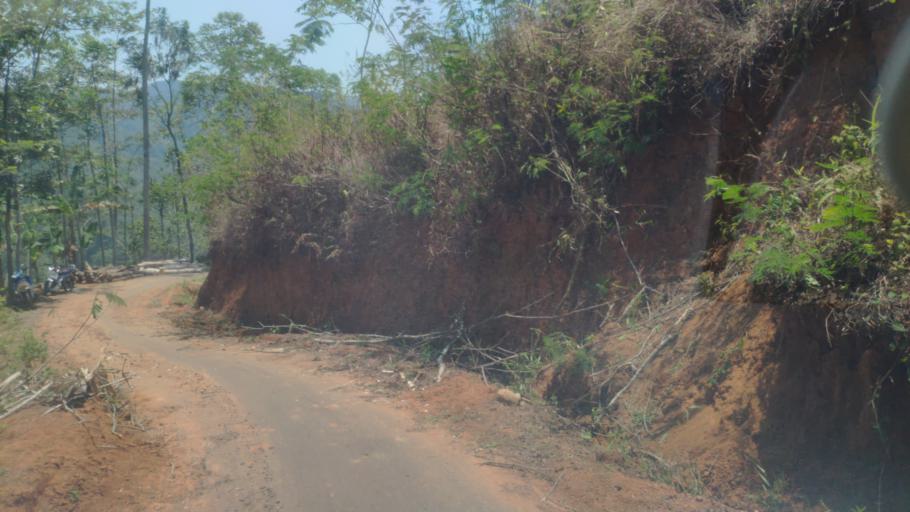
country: ID
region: Central Java
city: Buaran
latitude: -7.2860
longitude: 109.5896
